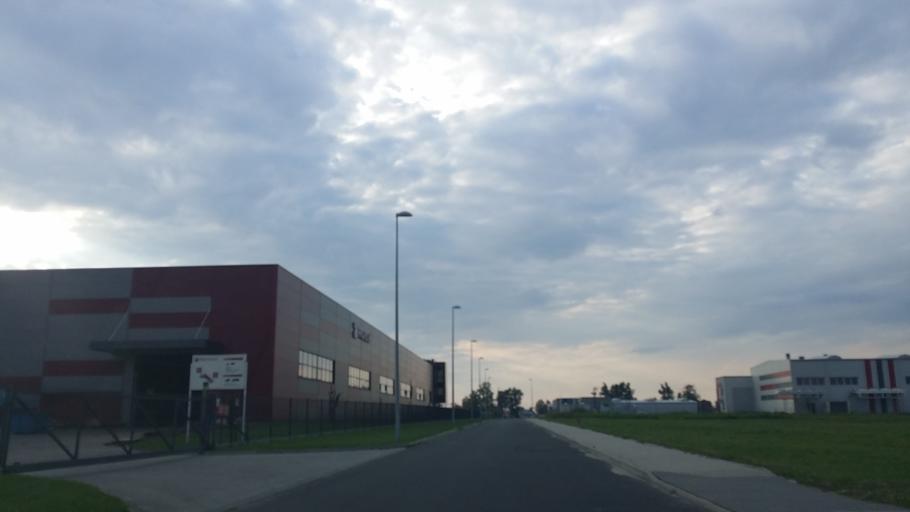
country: PL
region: Lesser Poland Voivodeship
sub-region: Powiat oswiecimski
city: Zator
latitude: 49.9943
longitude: 19.4195
